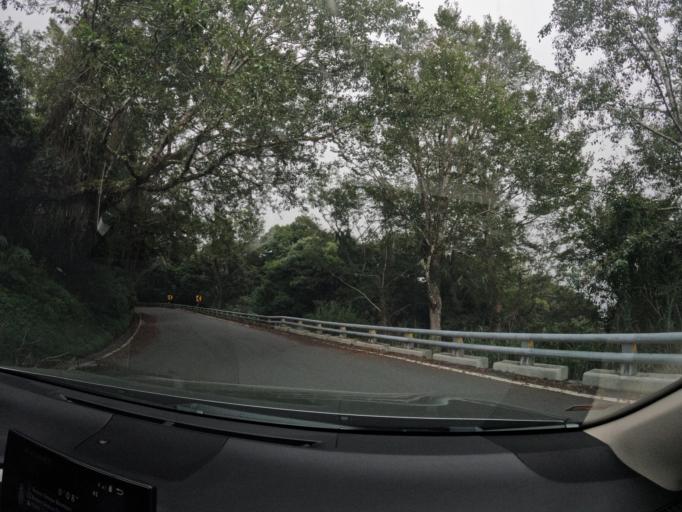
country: TW
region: Taiwan
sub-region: Taitung
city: Taitung
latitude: 23.2377
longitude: 120.9842
